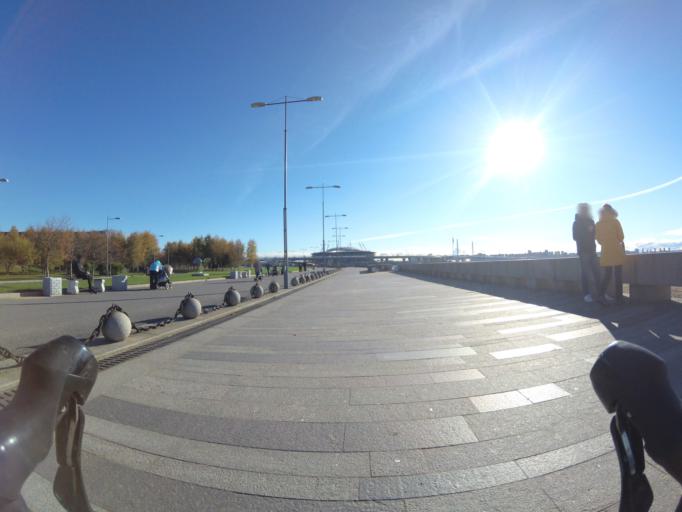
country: RU
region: Leningrad
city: Untolovo
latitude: 59.9807
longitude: 30.2030
